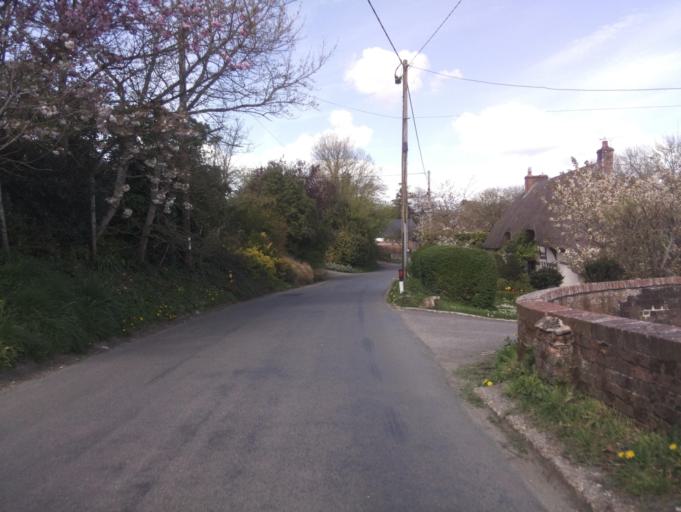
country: GB
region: England
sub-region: Hampshire
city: Abbotts Ann
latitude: 51.1291
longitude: -1.4922
